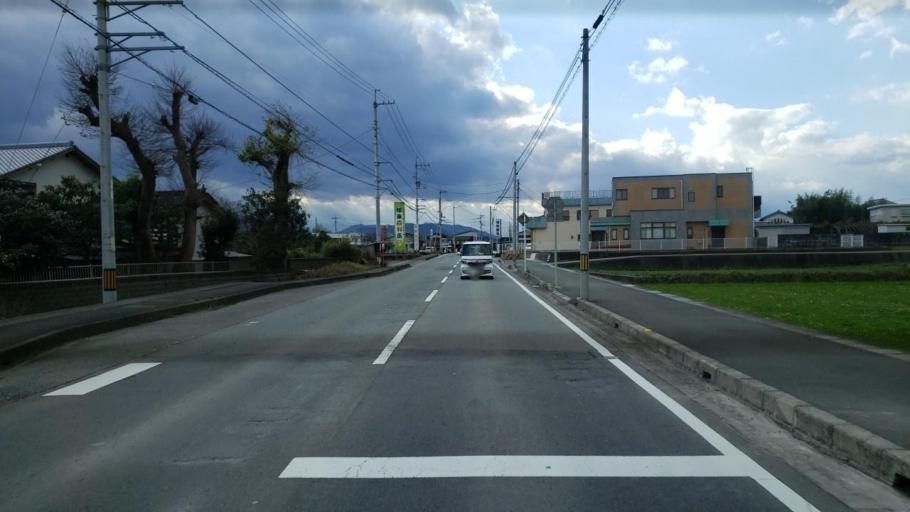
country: JP
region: Tokushima
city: Kamojimacho-jogejima
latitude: 34.0820
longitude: 134.2691
